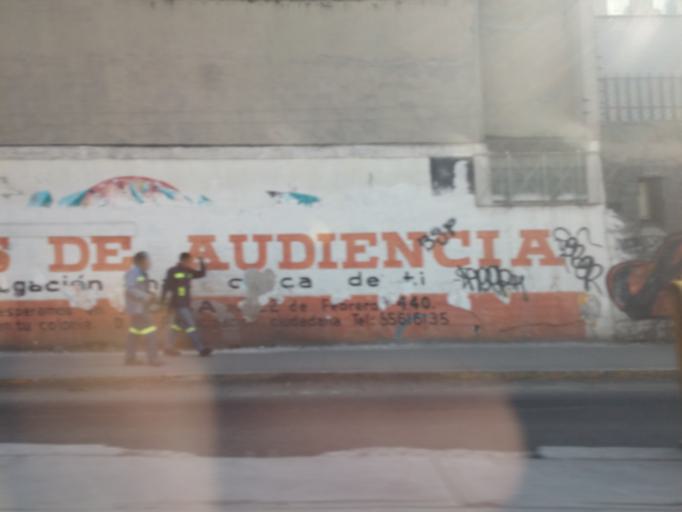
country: MX
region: Mexico City
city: Azcapotzalco
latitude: 19.4910
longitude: -99.1722
